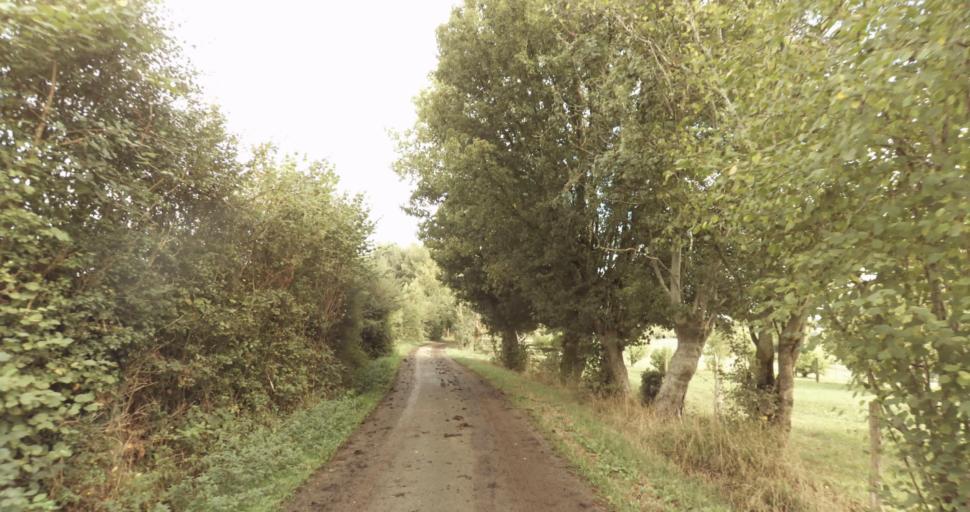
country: FR
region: Lower Normandy
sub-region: Departement de l'Orne
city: Gace
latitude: 48.8107
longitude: 0.2520
